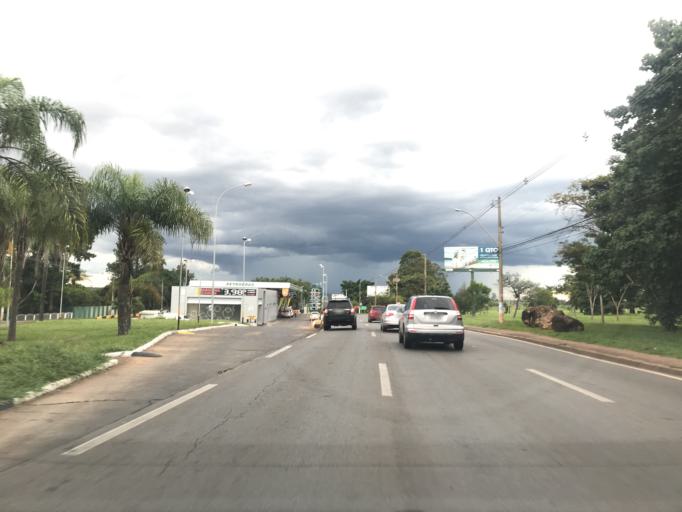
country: BR
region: Federal District
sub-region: Brasilia
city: Brasilia
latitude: -15.7223
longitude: -47.8899
